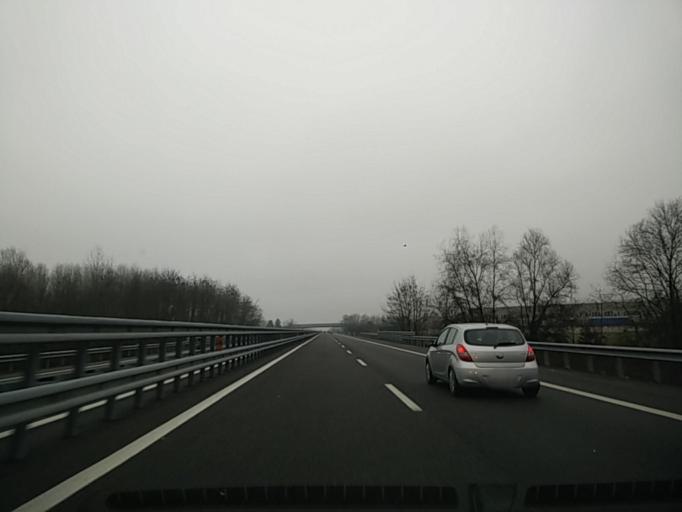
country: IT
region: Piedmont
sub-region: Provincia di Asti
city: Villafranca d'Asti
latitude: 44.9250
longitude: 8.0156
